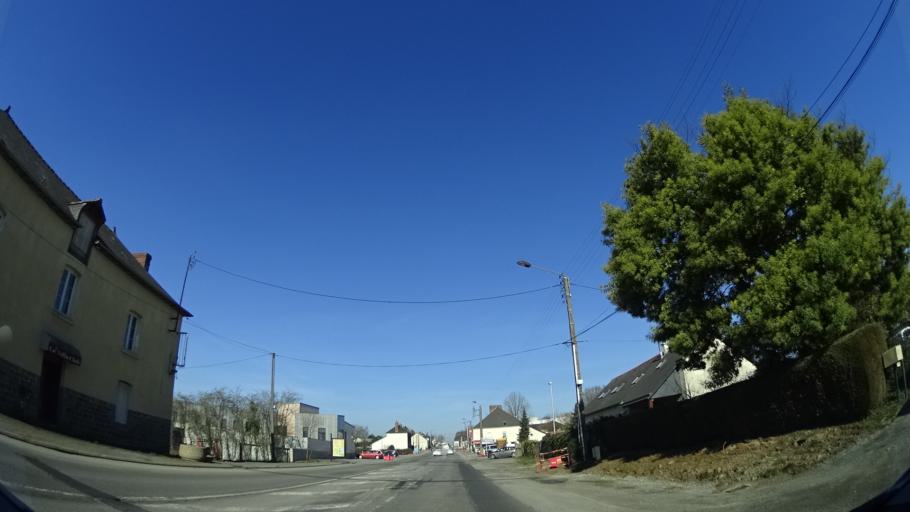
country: FR
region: Brittany
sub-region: Departement d'Ille-et-Vilaine
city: La Meziere
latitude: 48.2169
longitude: -1.7467
